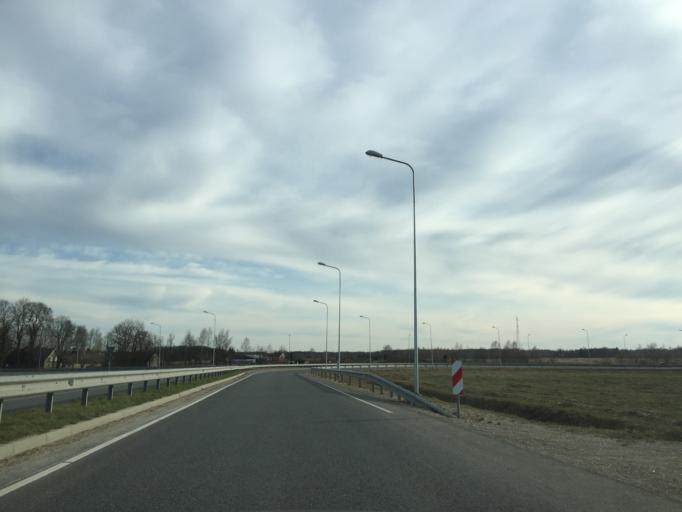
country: LV
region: Lielvarde
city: Lielvarde
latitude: 56.8078
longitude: 24.8857
